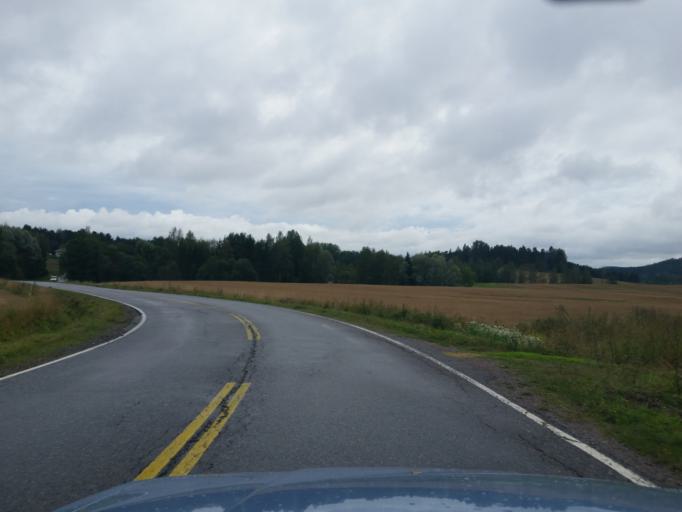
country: FI
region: Uusimaa
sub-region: Helsinki
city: Kaerkoelae
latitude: 60.5069
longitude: 23.9638
